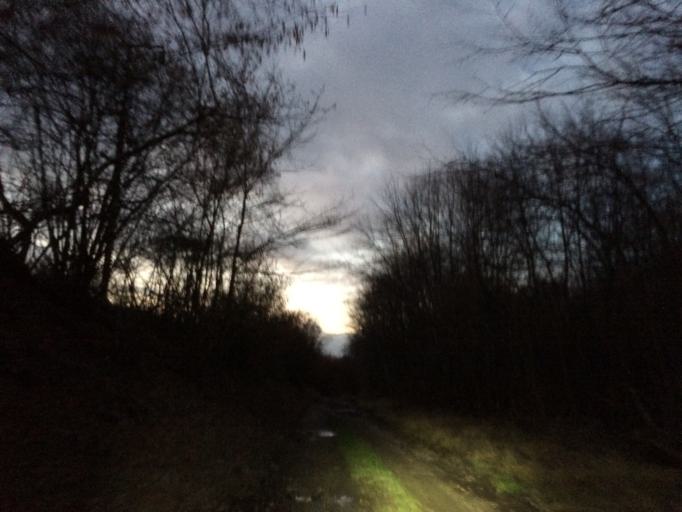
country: FR
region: Picardie
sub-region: Departement de l'Oise
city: Coye-la-Foret
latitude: 49.1431
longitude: 2.4863
